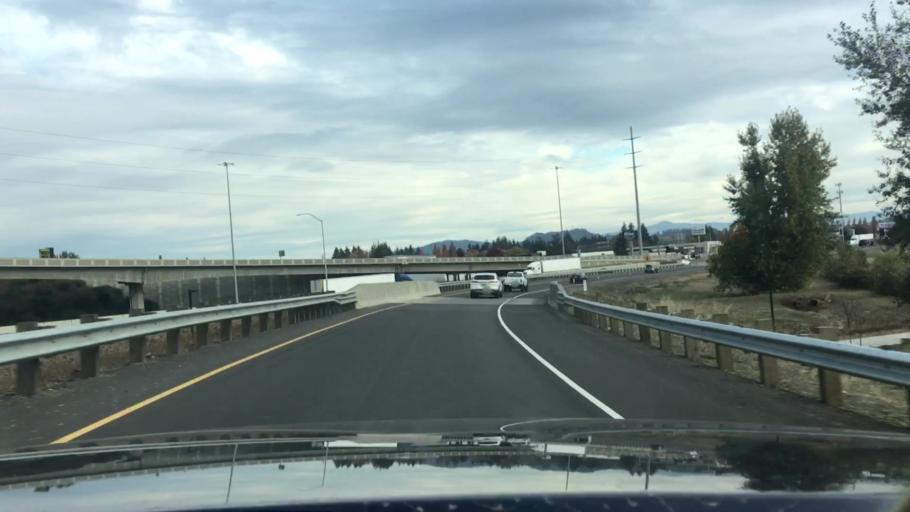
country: US
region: Oregon
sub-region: Lane County
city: Springfield
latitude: 44.0829
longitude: -123.0484
